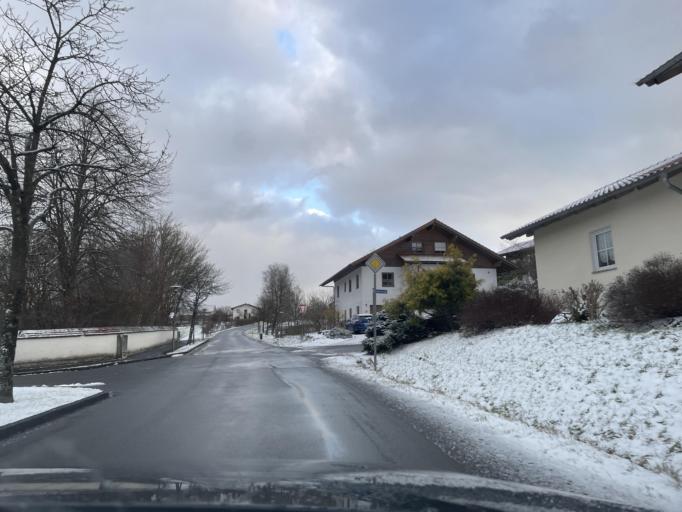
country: DE
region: Bavaria
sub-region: Lower Bavaria
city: Viechtach
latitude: 49.0887
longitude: 12.8795
